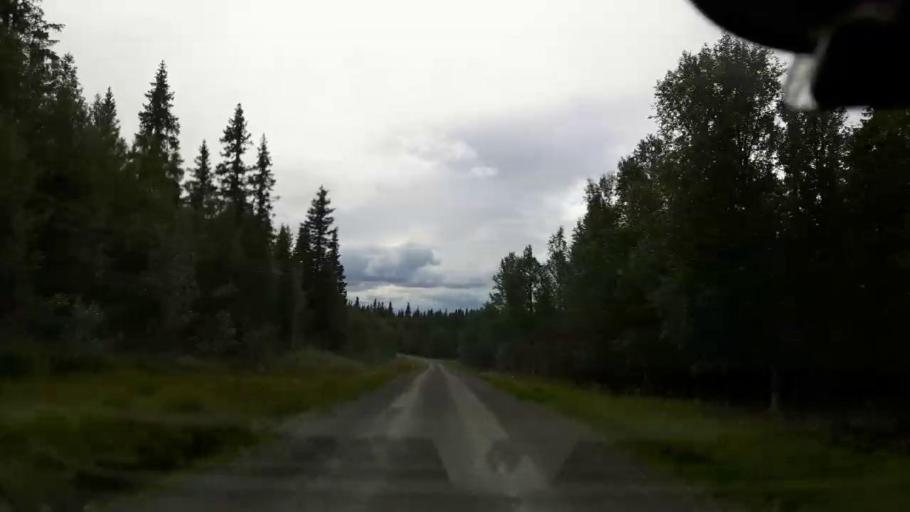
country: SE
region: Jaemtland
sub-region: Krokoms Kommun
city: Valla
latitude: 63.7605
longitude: 13.8370
